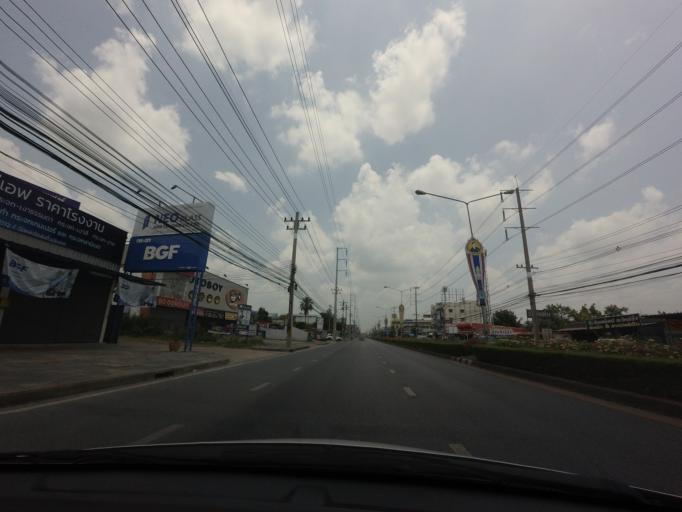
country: TH
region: Pathum Thani
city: Pathum Thani
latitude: 14.0378
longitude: 100.5252
